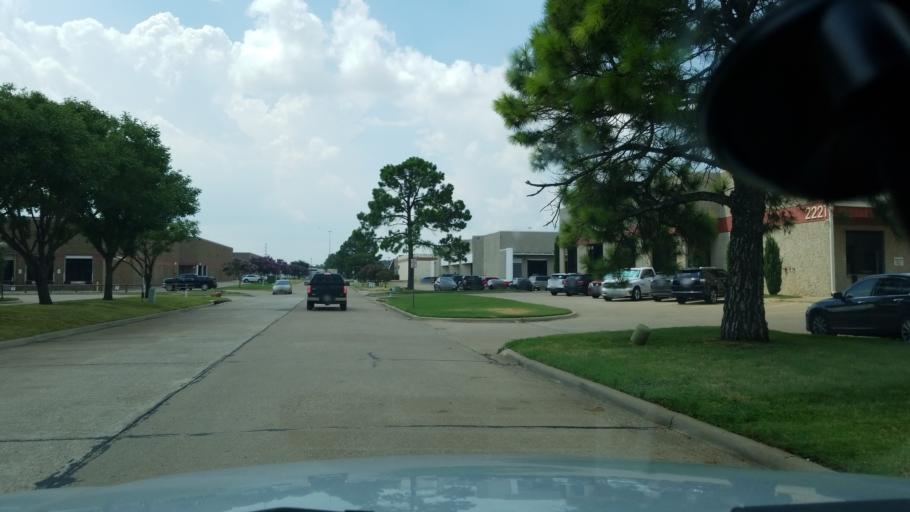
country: US
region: Texas
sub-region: Dallas County
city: Irving
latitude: 32.8414
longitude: -96.8986
